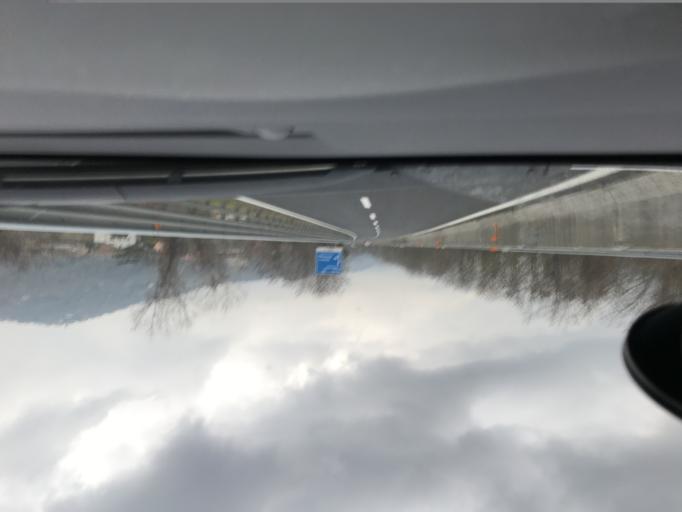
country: IT
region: The Marches
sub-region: Provincia di Ancona
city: Macine-Borgo Loreto
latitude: 43.4831
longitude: 13.0924
